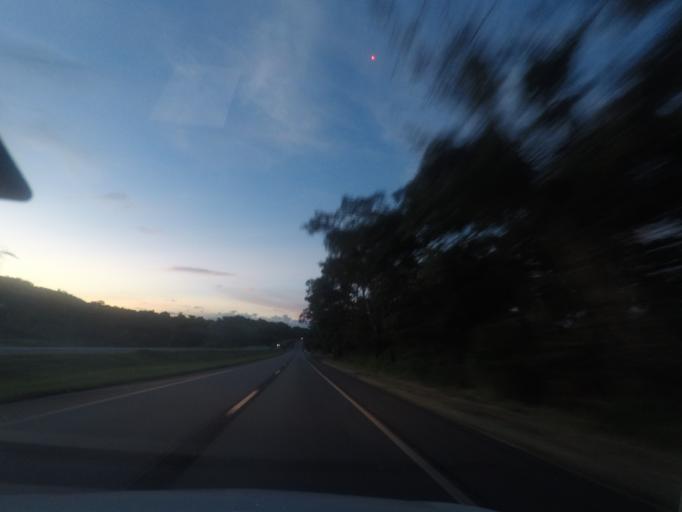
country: BR
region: Goias
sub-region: Pontalina
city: Pontalina
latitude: -17.4476
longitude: -49.2289
